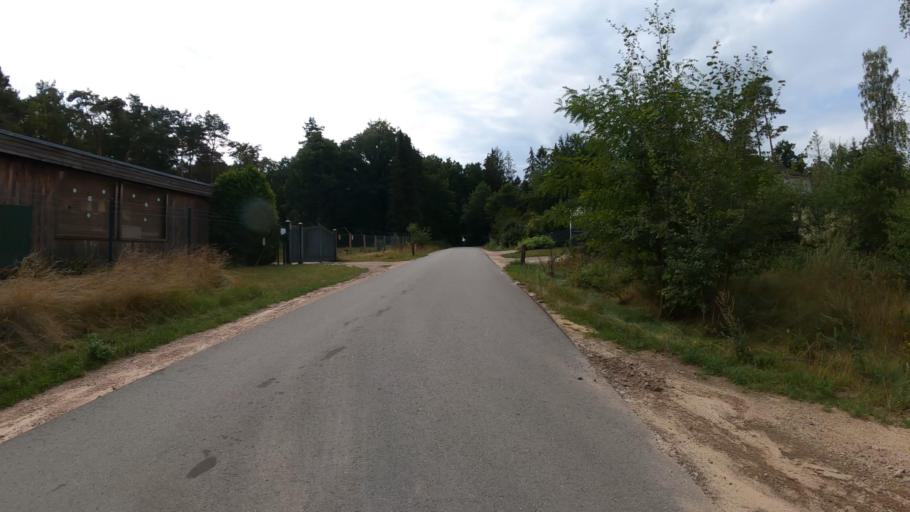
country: DE
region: Lower Saxony
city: Wenzendorf
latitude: 53.3626
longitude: 9.7561
